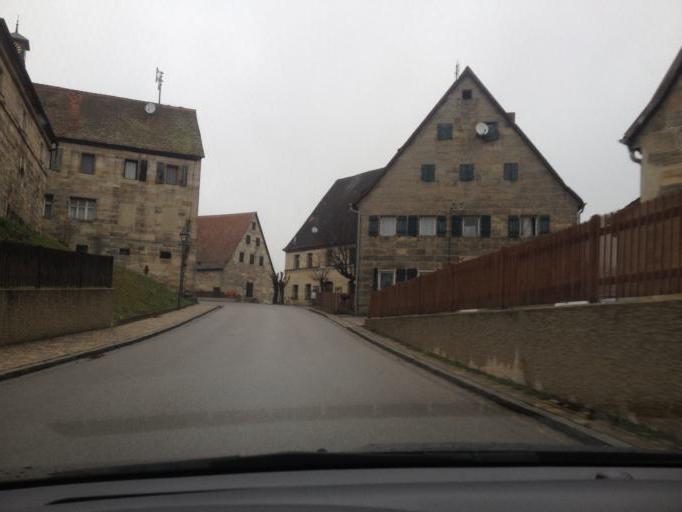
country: DE
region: Bavaria
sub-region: Regierungsbezirk Mittelfranken
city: Lauf an der Pegnitz
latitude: 49.5511
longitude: 11.2692
